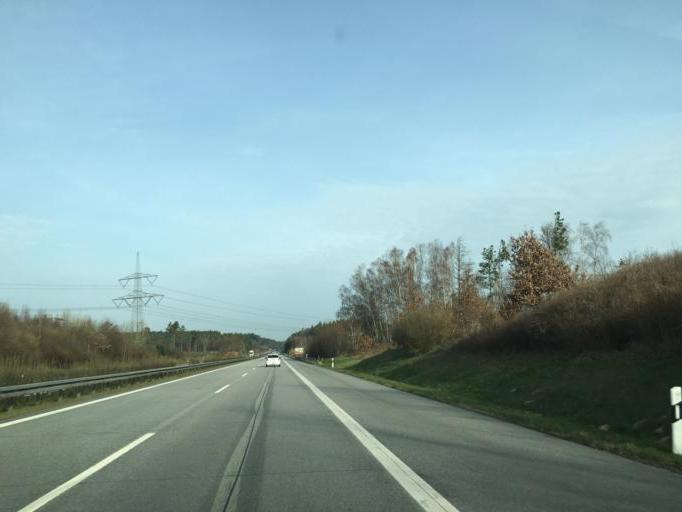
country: DE
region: Mecklenburg-Vorpommern
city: Malchow
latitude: 53.4394
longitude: 12.4087
